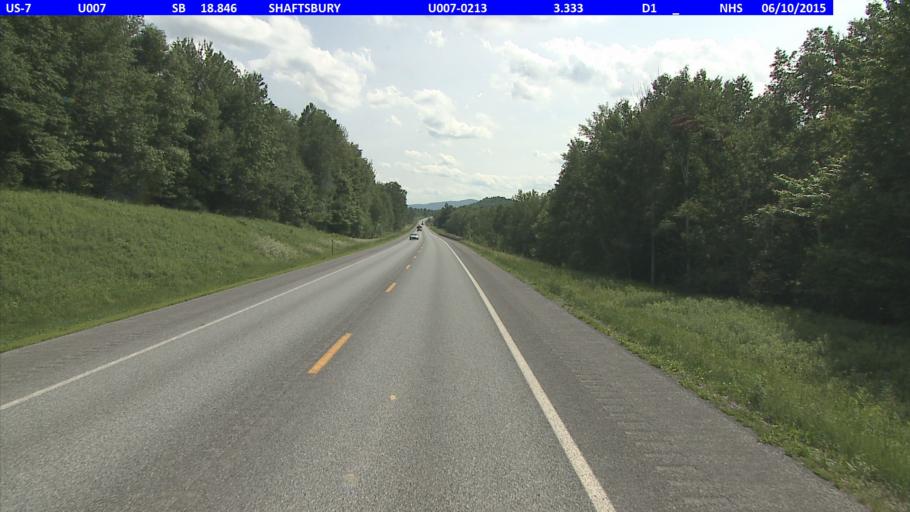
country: US
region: Vermont
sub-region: Bennington County
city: North Bennington
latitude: 42.9750
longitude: -73.1590
